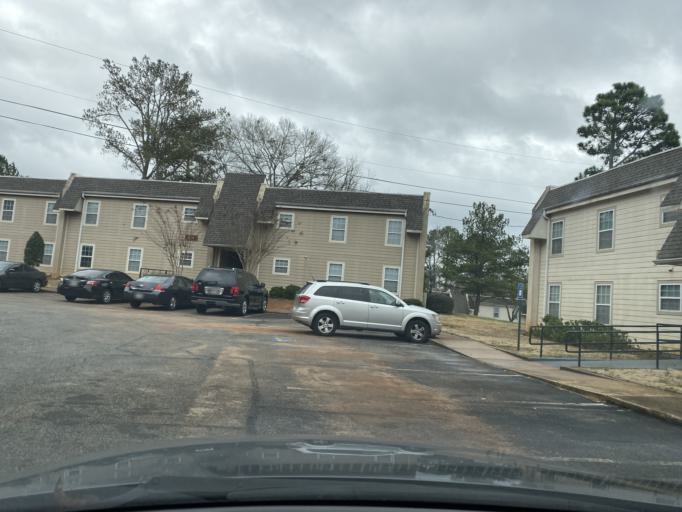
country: US
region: Georgia
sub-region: DeKalb County
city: Pine Mountain
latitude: 33.6986
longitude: -84.1456
